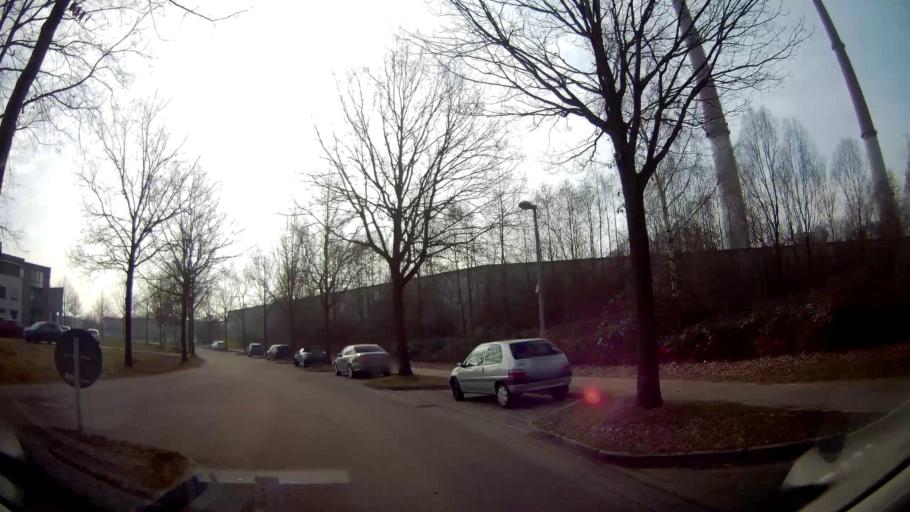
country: DE
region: North Rhine-Westphalia
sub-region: Regierungsbezirk Munster
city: Gladbeck
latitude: 51.5735
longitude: 6.9371
